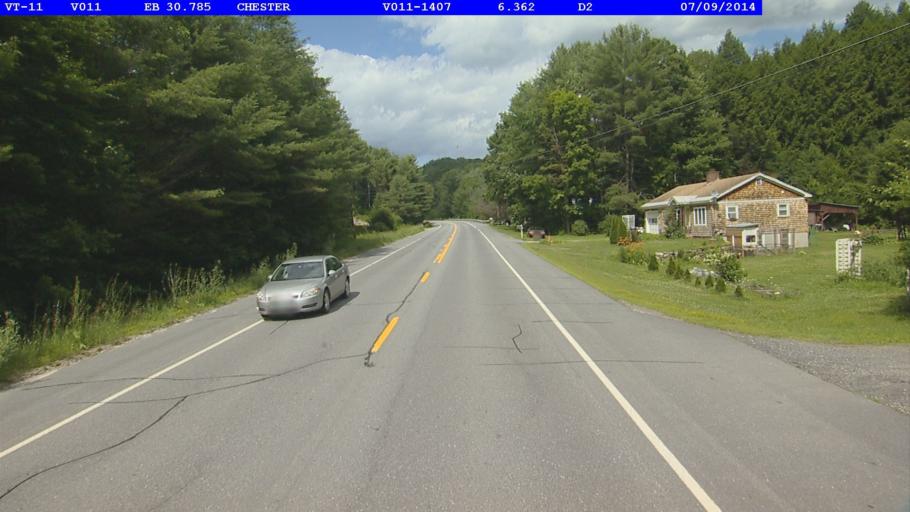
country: US
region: Vermont
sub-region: Windsor County
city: Chester
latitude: 43.2698
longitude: -72.5720
